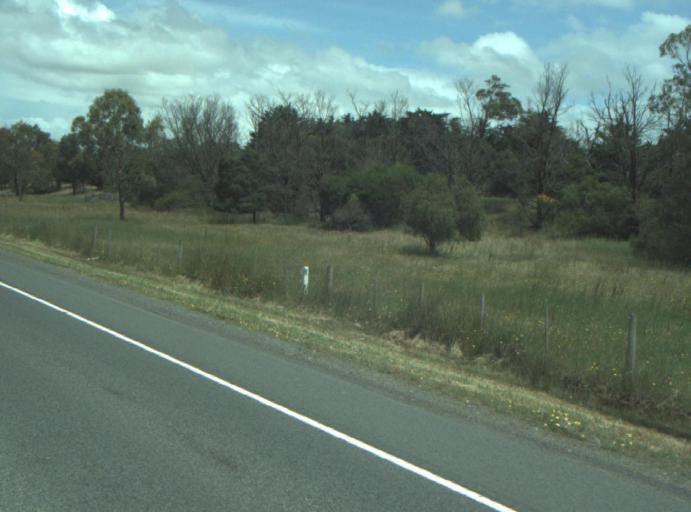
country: AU
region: Victoria
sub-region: Greater Geelong
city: Wandana Heights
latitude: -38.2375
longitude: 144.2789
